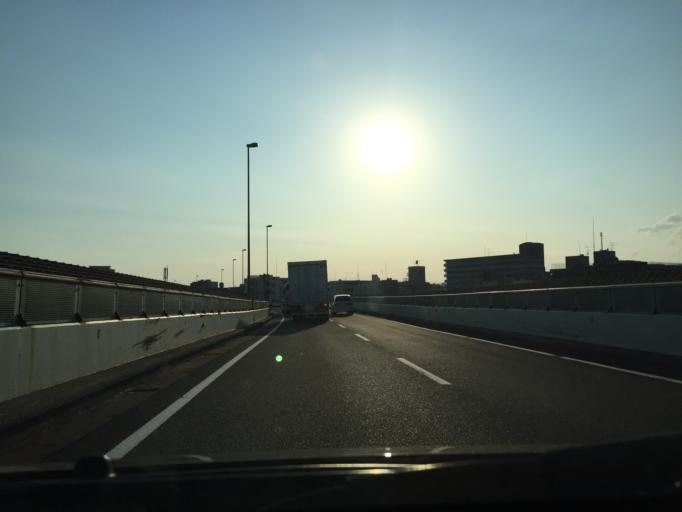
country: JP
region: Kanagawa
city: Yokohama
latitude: 35.4370
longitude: 139.6374
